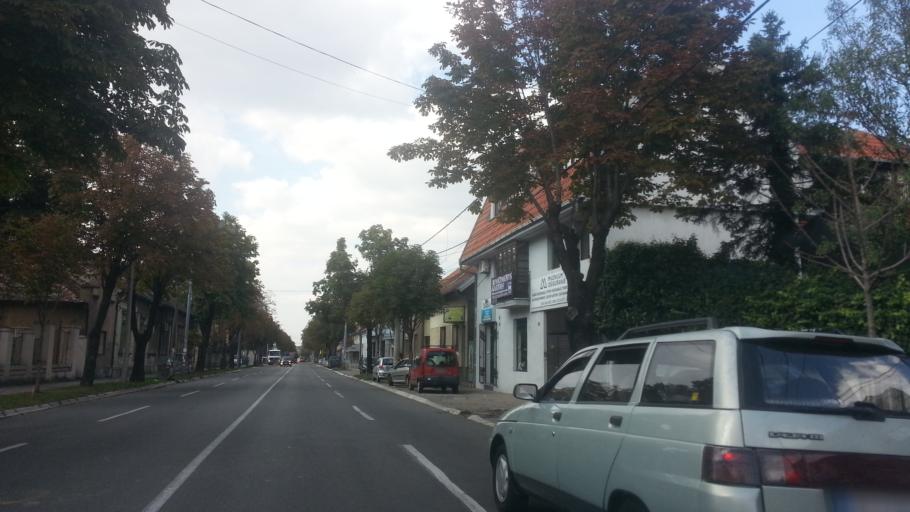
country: RS
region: Central Serbia
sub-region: Belgrade
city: Zemun
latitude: 44.8496
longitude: 20.4015
